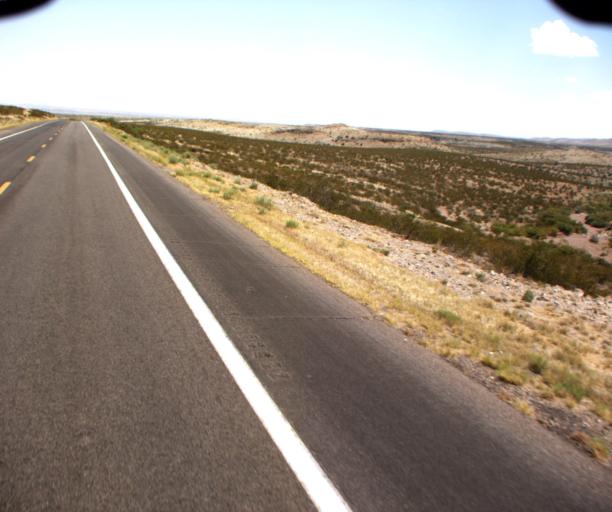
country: US
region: Arizona
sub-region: Greenlee County
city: Clifton
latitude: 32.7327
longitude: -109.1910
